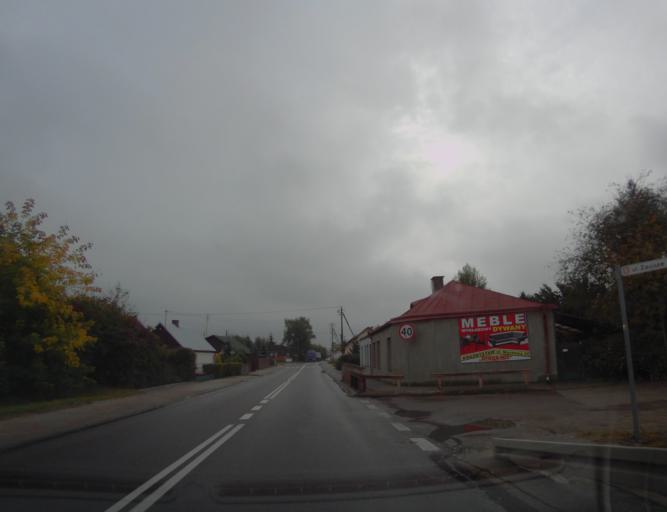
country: PL
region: Lublin Voivodeship
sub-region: Powiat chelmski
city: Rejowiec
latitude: 51.0909
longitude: 23.2818
